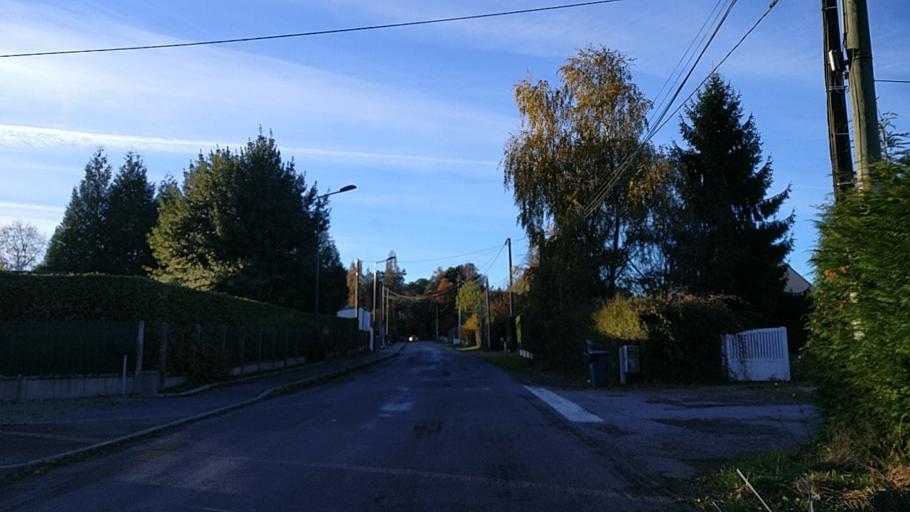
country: FR
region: Brittany
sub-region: Departement d'Ille-et-Vilaine
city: Liffre
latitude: 48.1885
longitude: -1.5210
